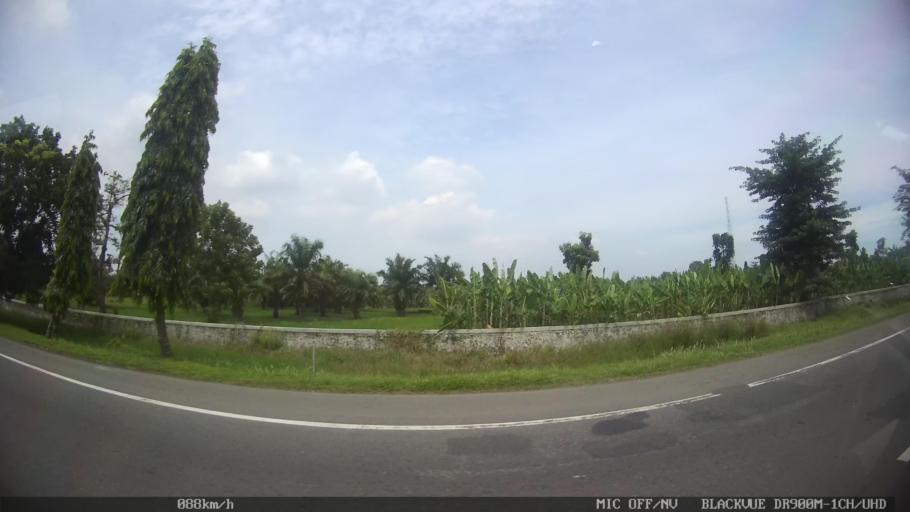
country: ID
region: North Sumatra
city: Labuhan Deli
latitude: 3.6990
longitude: 98.6817
